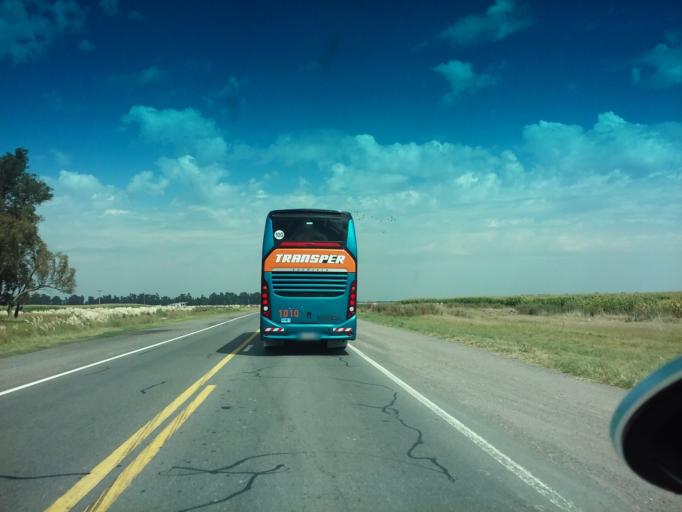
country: AR
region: Buenos Aires
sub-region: Partido de Carlos Casares
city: Carlos Casares
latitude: -35.6587
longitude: -61.4026
